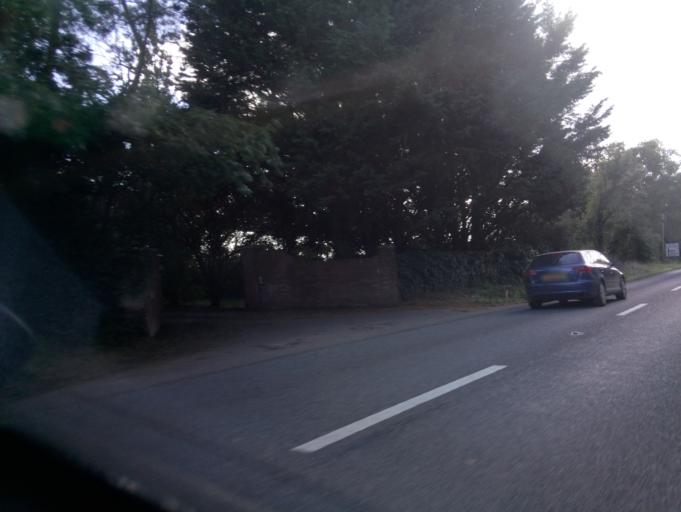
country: GB
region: England
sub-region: Devon
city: Newton Poppleford
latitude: 50.7061
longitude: -3.3763
